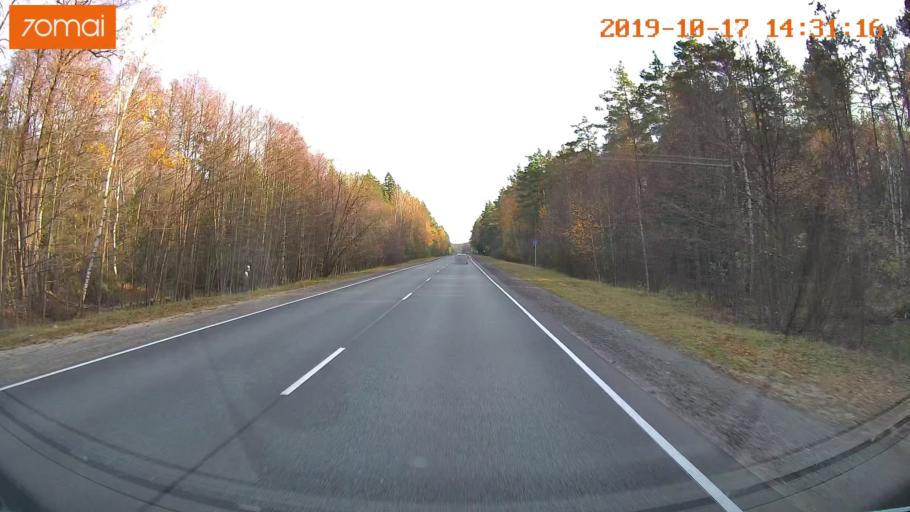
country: RU
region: Rjazan
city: Solotcha
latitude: 54.9382
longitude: 39.9590
